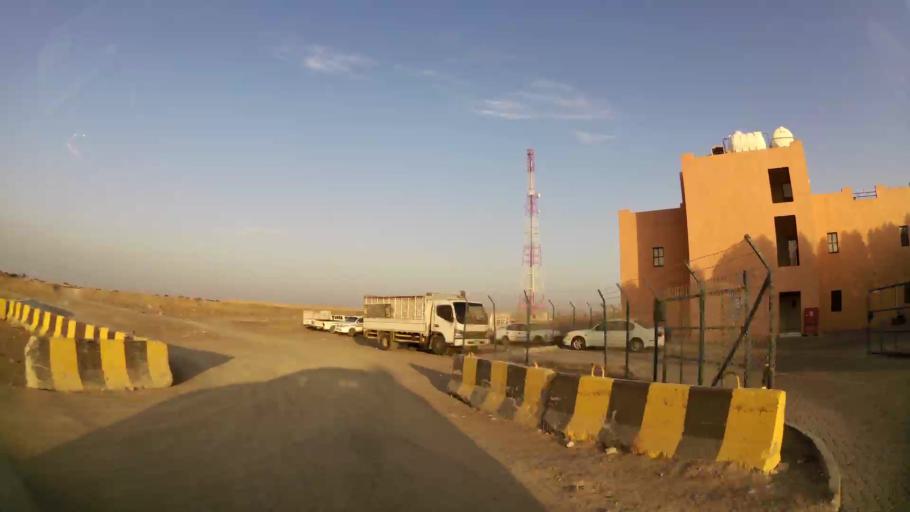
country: AE
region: Abu Dhabi
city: Al Ain
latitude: 24.1637
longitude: 55.8174
